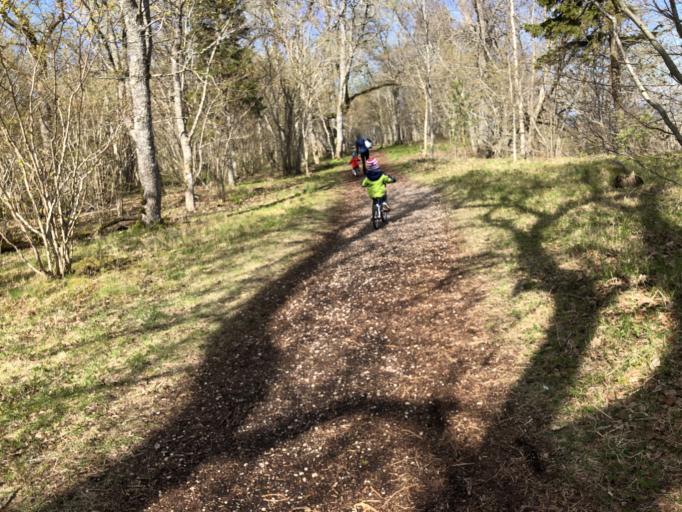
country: EE
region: Harju
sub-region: Harku vald
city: Tabasalu
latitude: 59.4407
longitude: 24.5303
